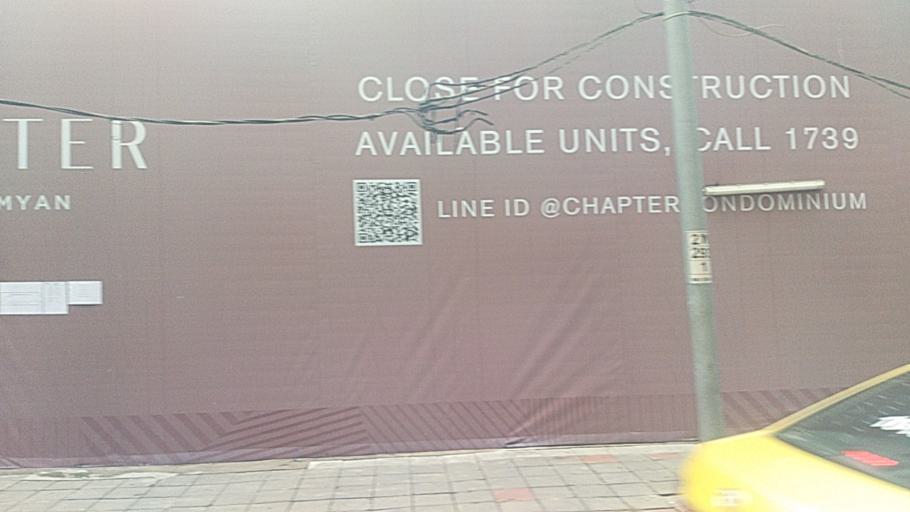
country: TH
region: Bangkok
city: Bang Rak
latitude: 13.7314
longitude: 100.5233
